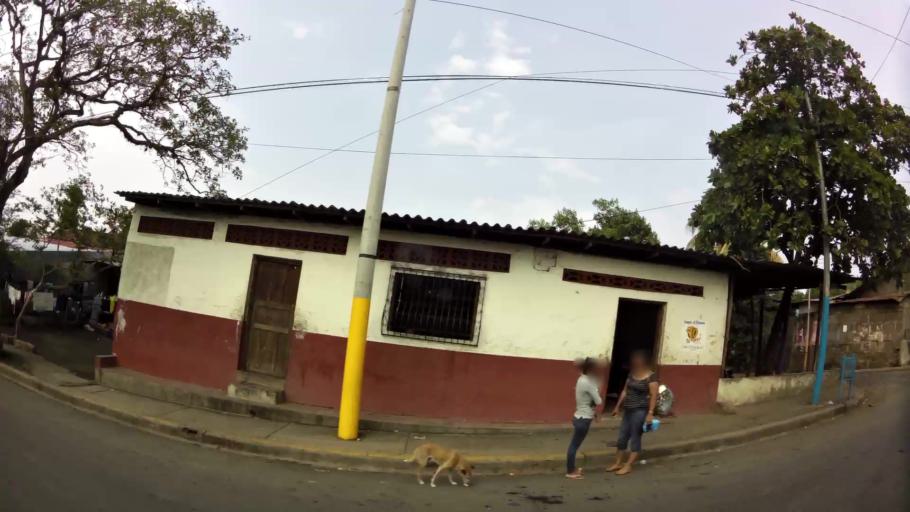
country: NI
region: Masaya
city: Masaya
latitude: 11.9629
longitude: -86.0923
